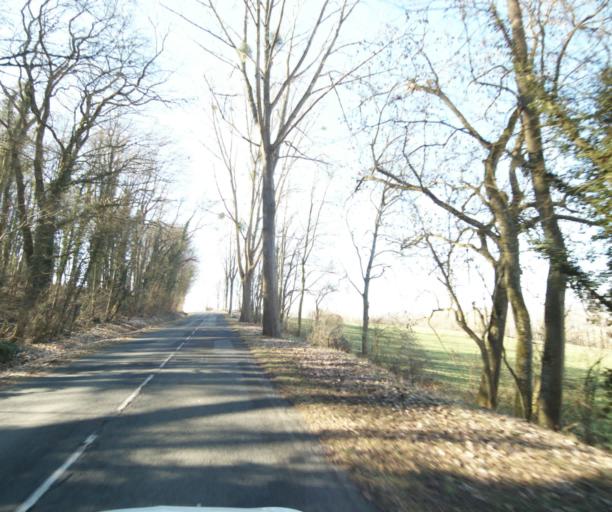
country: FR
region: Lorraine
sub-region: Departement de Meurthe-et-Moselle
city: Lay-Saint-Christophe
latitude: 48.7366
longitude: 6.1861
